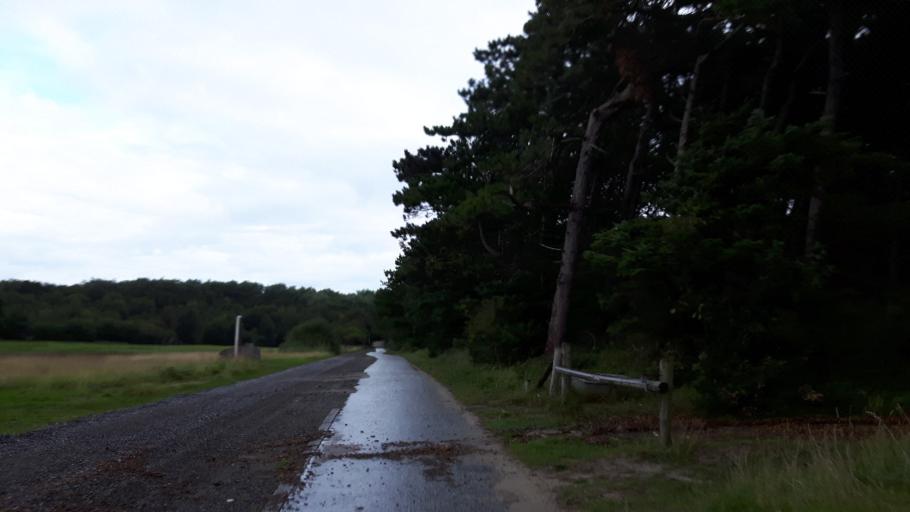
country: NL
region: Friesland
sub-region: Gemeente Ameland
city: Nes
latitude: 53.4509
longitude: 5.7571
